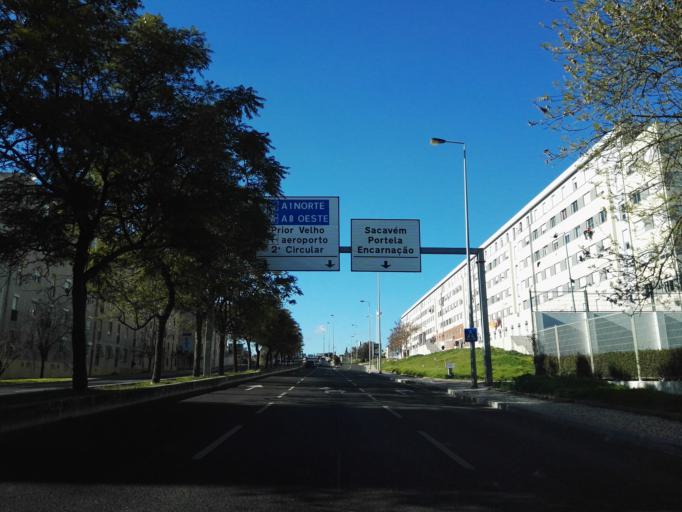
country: PT
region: Lisbon
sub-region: Loures
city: Moscavide
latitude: 38.7797
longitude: -9.1168
